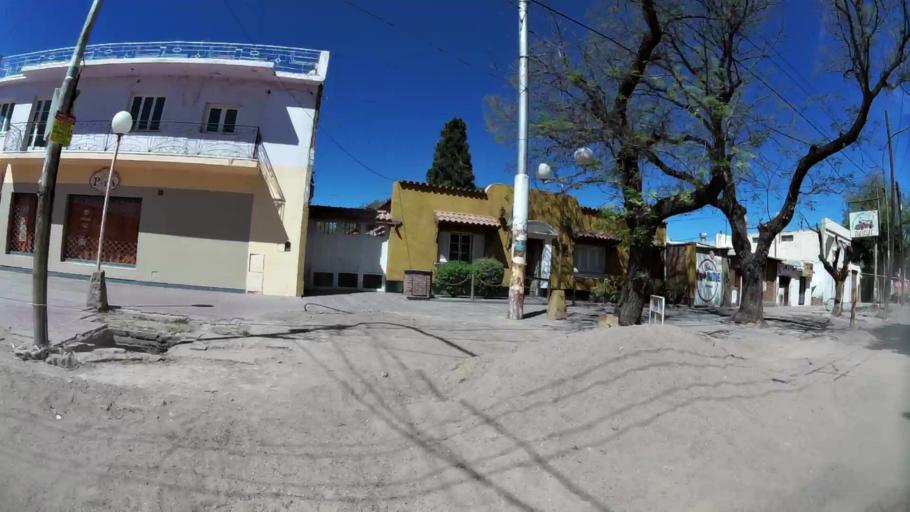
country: AR
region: Mendoza
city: Las Heras
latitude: -32.8527
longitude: -68.8343
